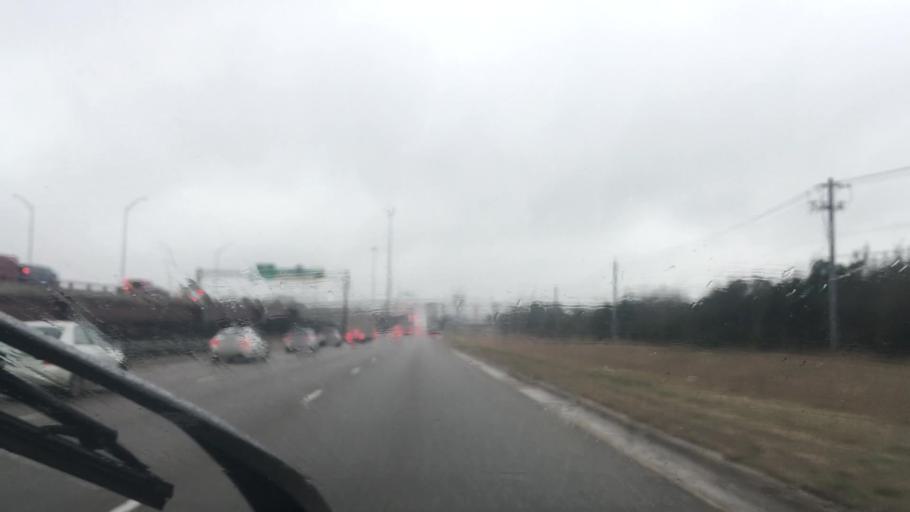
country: US
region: Texas
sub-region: Williamson County
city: Anderson Mill
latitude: 30.4722
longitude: -97.7866
